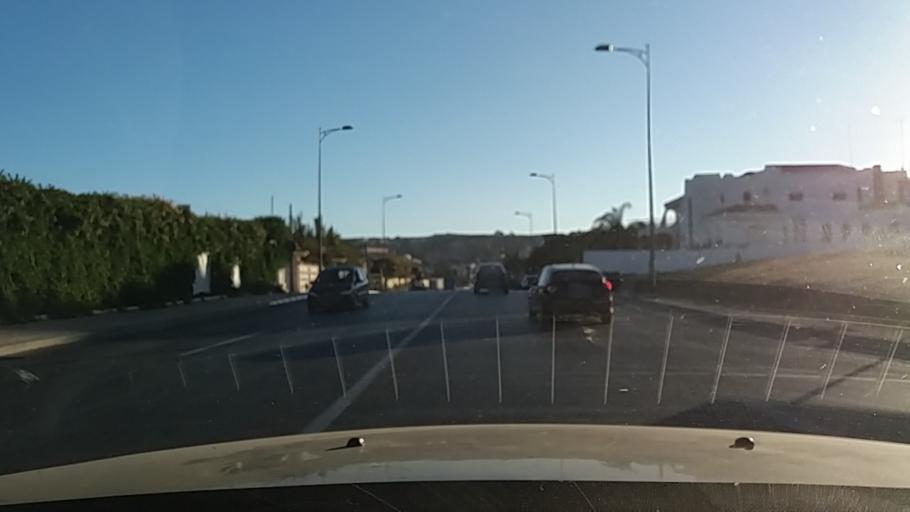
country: MA
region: Tanger-Tetouan
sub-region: Tanger-Assilah
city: Tangier
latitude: 35.7774
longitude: -5.8515
